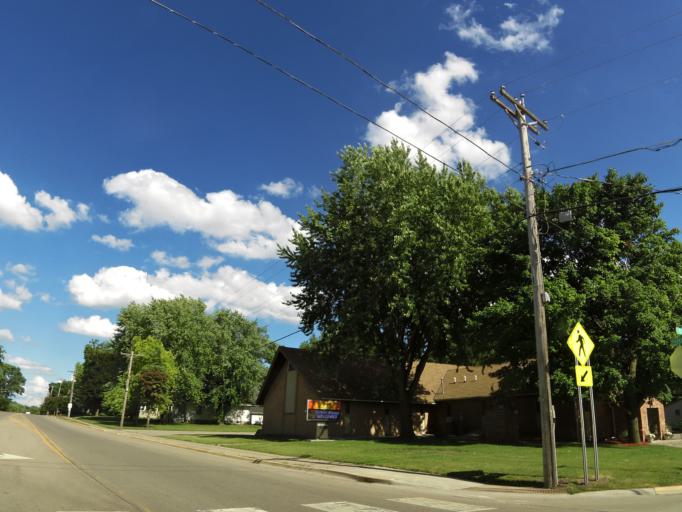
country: US
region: Minnesota
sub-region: Meeker County
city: Dassel
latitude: 45.0814
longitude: -94.3070
